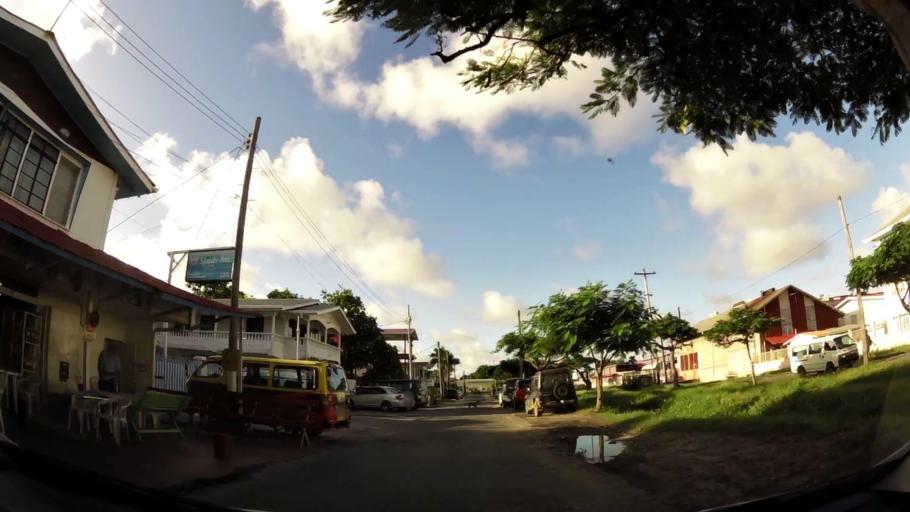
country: GY
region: Demerara-Mahaica
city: Georgetown
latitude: 6.8168
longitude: -58.1573
